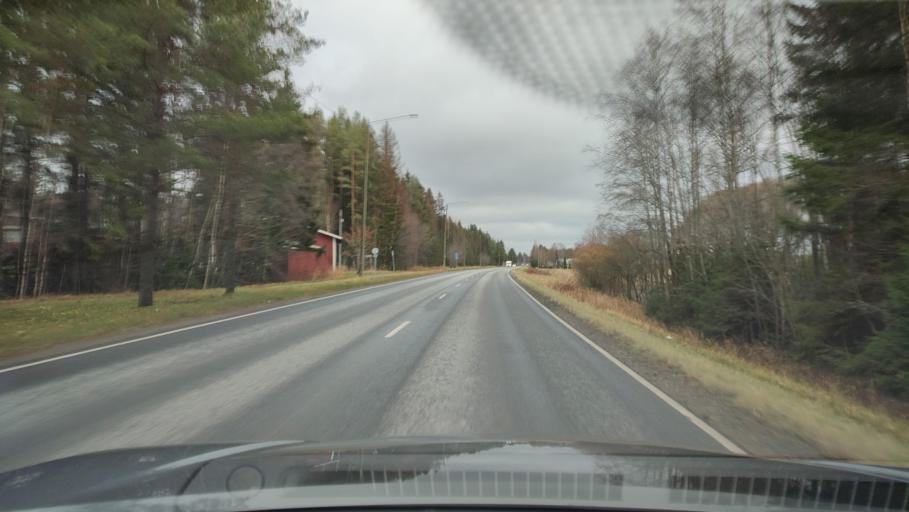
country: FI
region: Southern Ostrobothnia
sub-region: Suupohja
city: Kauhajoki
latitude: 62.4032
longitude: 22.1607
